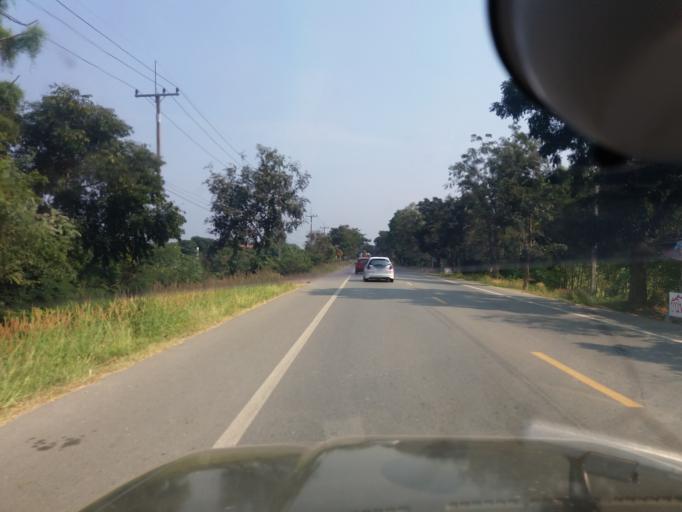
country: TH
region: Sing Buri
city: Bang Racham
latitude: 14.8826
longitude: 100.3534
